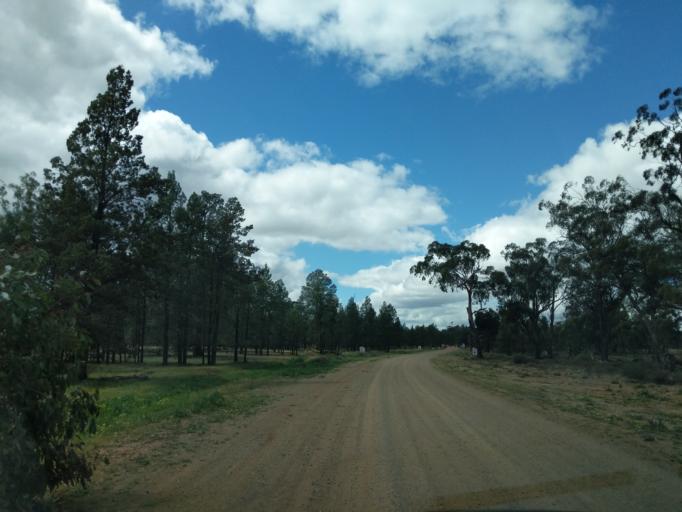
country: AU
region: New South Wales
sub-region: Coolamon
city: Coolamon
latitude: -34.8550
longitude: 146.9132
